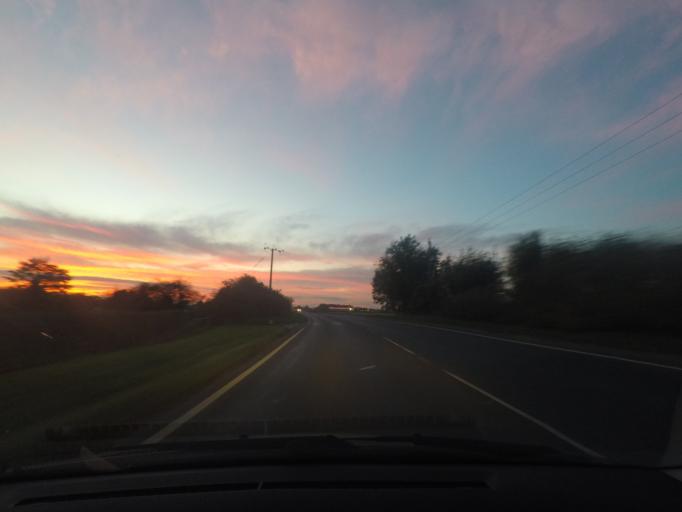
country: GB
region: England
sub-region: East Riding of Yorkshire
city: Pocklington
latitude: 53.9187
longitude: -0.7885
